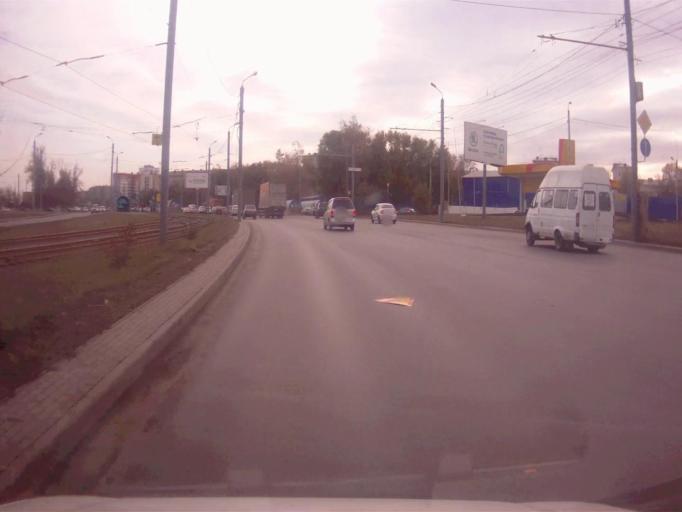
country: RU
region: Chelyabinsk
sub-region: Gorod Chelyabinsk
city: Chelyabinsk
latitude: 55.1503
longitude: 61.4422
